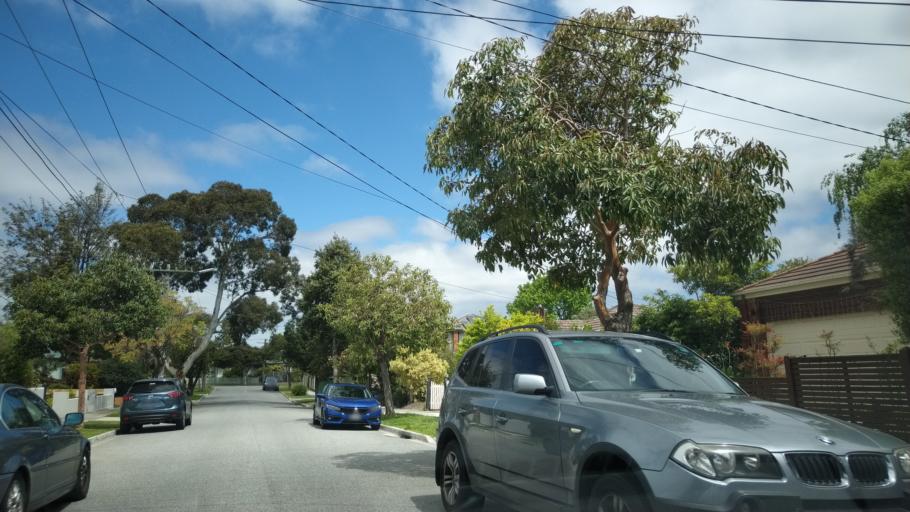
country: AU
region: Victoria
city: Murrumbeena
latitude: -37.8990
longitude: 145.0707
